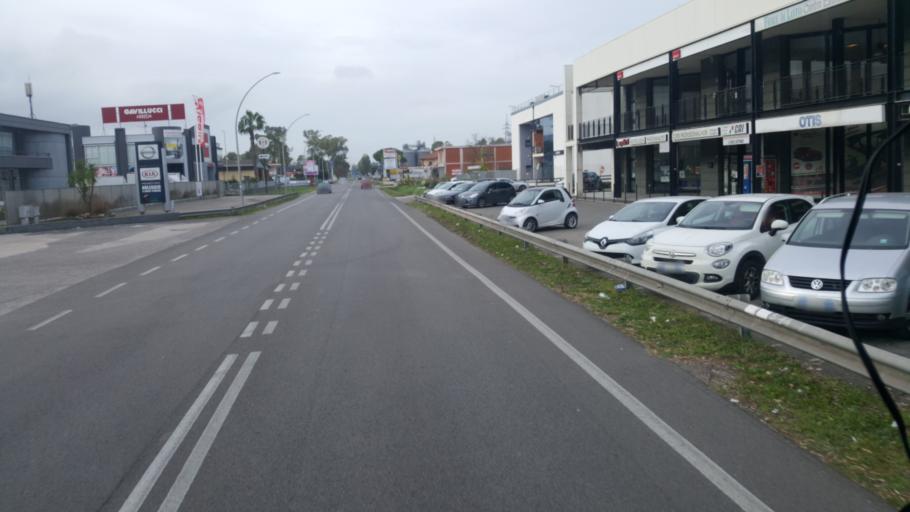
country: IT
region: Latium
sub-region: Provincia di Latina
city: Latina
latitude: 41.4764
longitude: 12.8787
